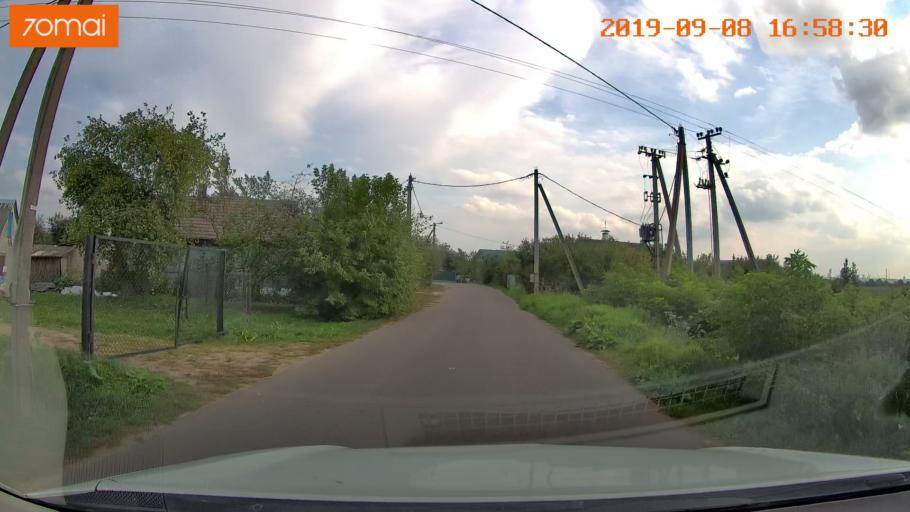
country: BY
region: Grodnenskaya
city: Hrodna
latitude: 53.7264
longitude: 23.9276
